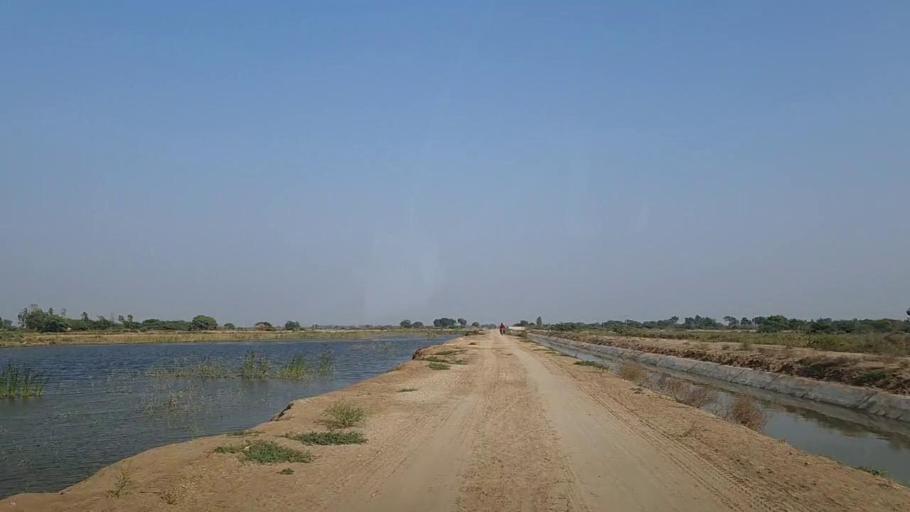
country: PK
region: Sindh
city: Mirpur Sakro
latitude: 24.6154
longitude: 67.7152
